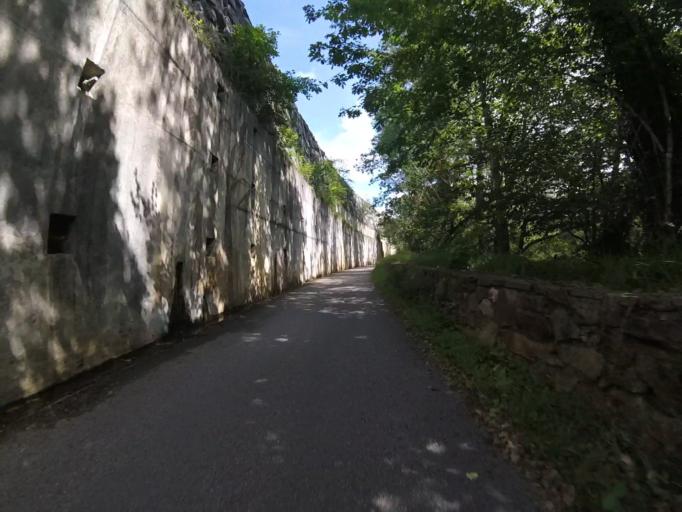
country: ES
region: Navarre
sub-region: Provincia de Navarra
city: Igantzi
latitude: 43.2362
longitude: -1.6767
